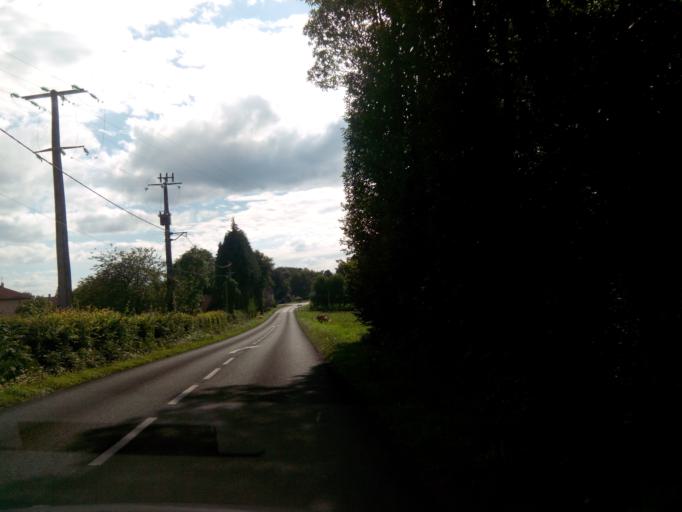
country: FR
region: Limousin
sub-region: Departement de la Haute-Vienne
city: Saint-Leonard-de-Noblat
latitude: 45.8246
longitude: 1.5358
